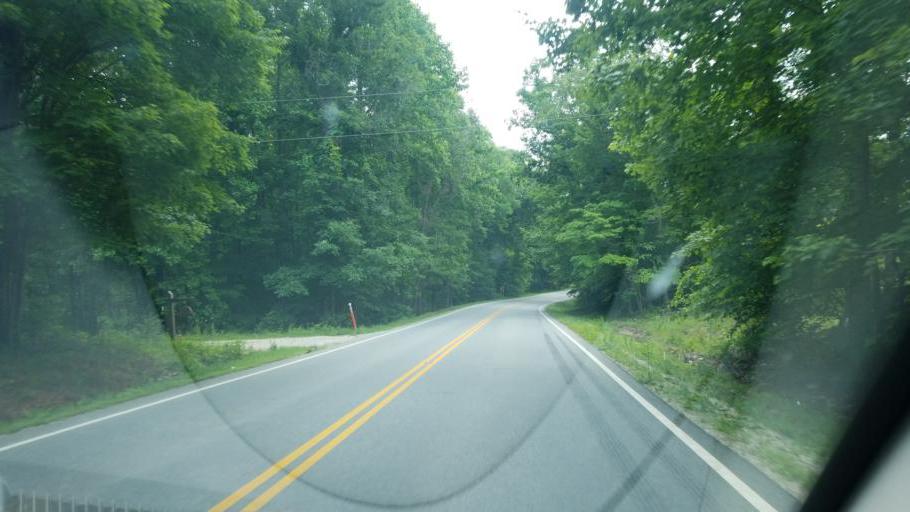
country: US
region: Virginia
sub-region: Appomattox County
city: Appomattox
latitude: 37.5479
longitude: -78.8326
